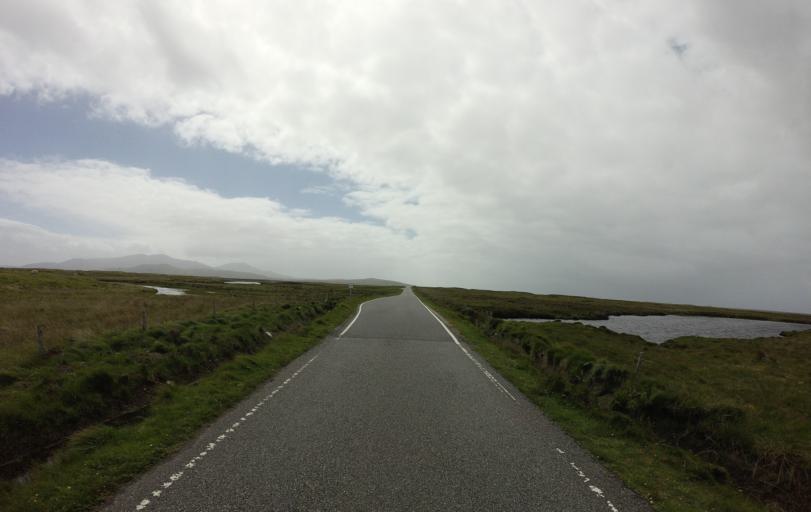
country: GB
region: Scotland
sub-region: Eilean Siar
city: Benbecula
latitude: 57.3787
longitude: -7.3434
